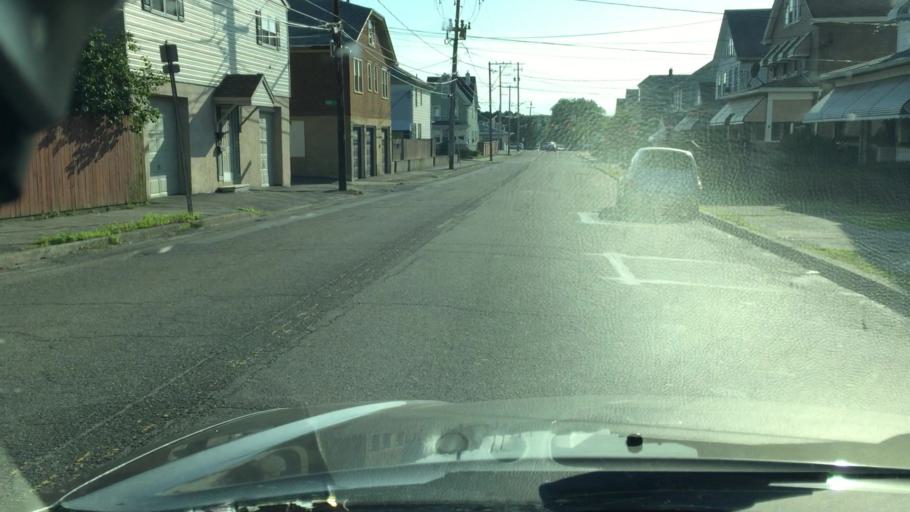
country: US
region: Pennsylvania
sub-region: Luzerne County
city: West Hazleton
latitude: 40.9652
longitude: -75.9948
